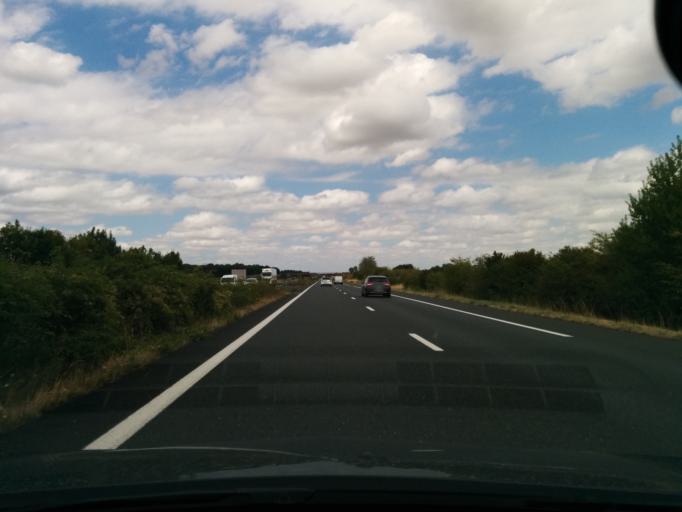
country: FR
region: Centre
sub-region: Departement de l'Indre
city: Luant
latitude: 46.6684
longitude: 1.5743
